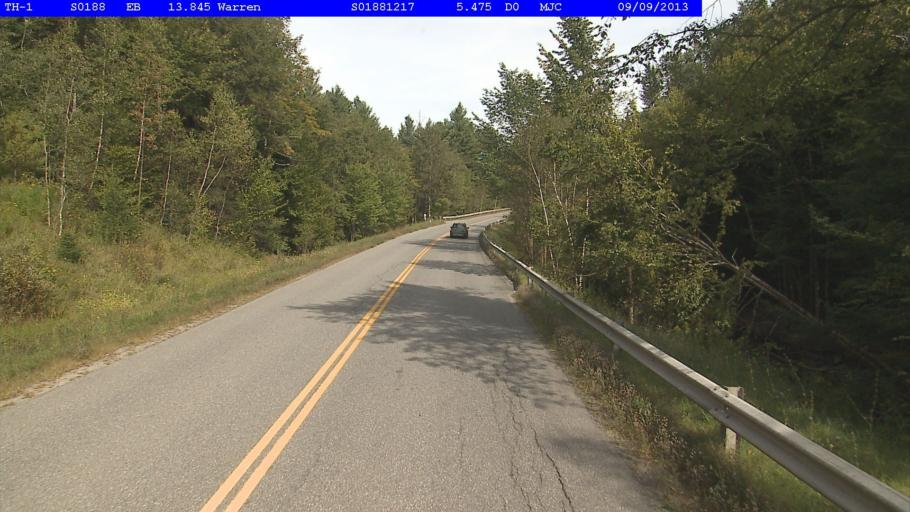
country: US
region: Vermont
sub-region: Washington County
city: Northfield
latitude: 44.1064
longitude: -72.8358
